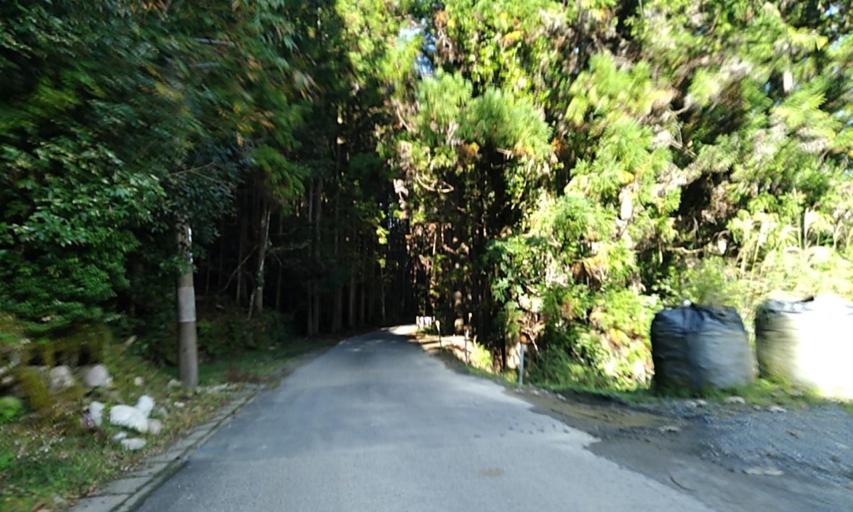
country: JP
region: Wakayama
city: Shingu
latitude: 33.9156
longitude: 135.9894
